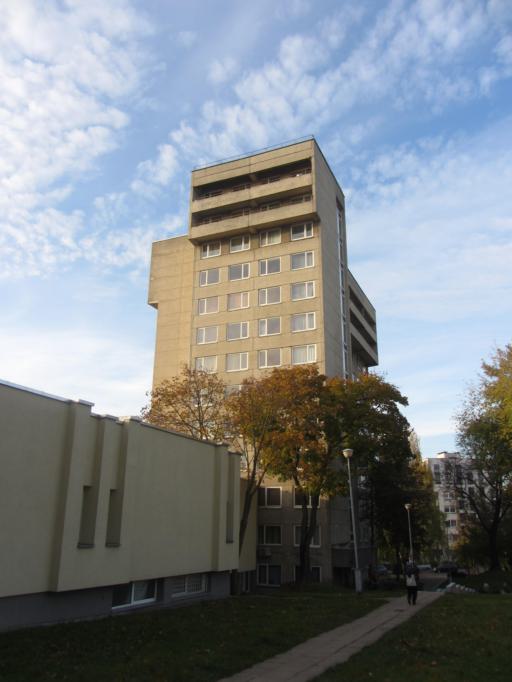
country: LT
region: Vilnius County
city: Naujamiestis
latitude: 54.6773
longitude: 25.2608
